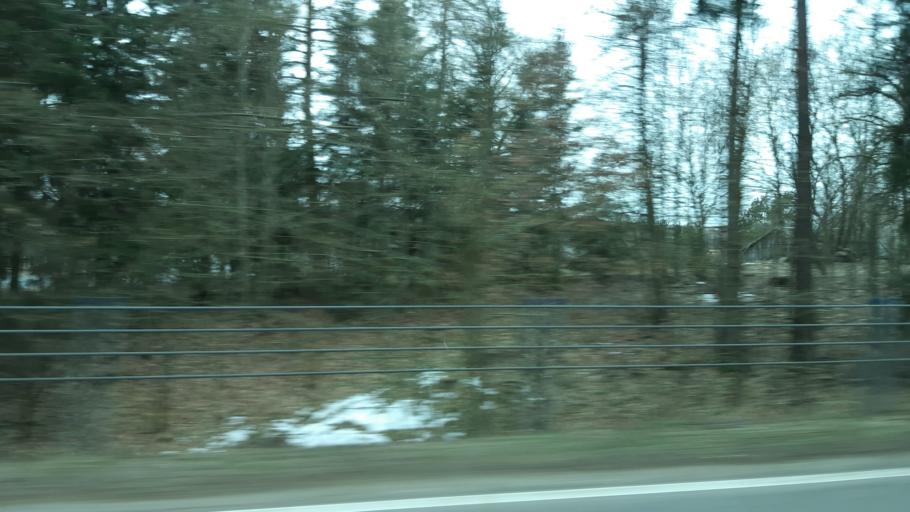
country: PL
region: Podlasie
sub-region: Suwalki
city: Suwalki
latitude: 54.3114
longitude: 22.9578
